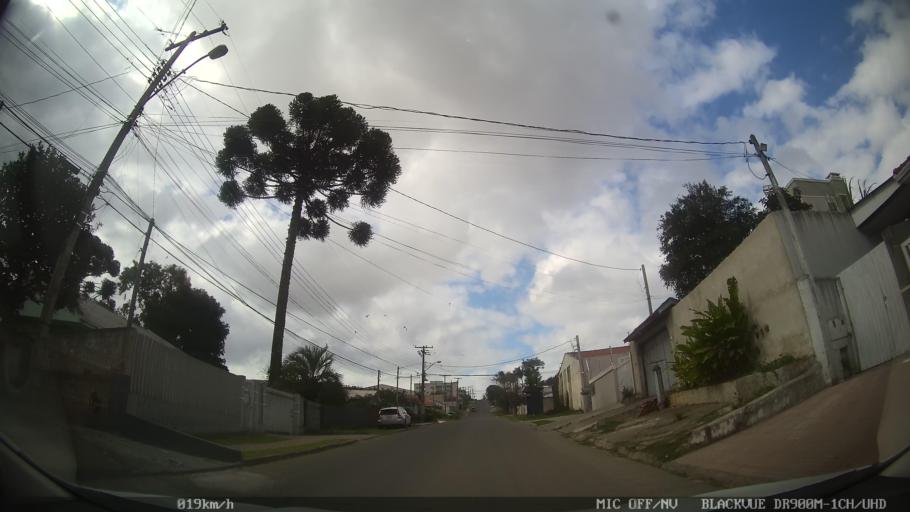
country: BR
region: Parana
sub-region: Colombo
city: Colombo
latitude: -25.3573
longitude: -49.2059
